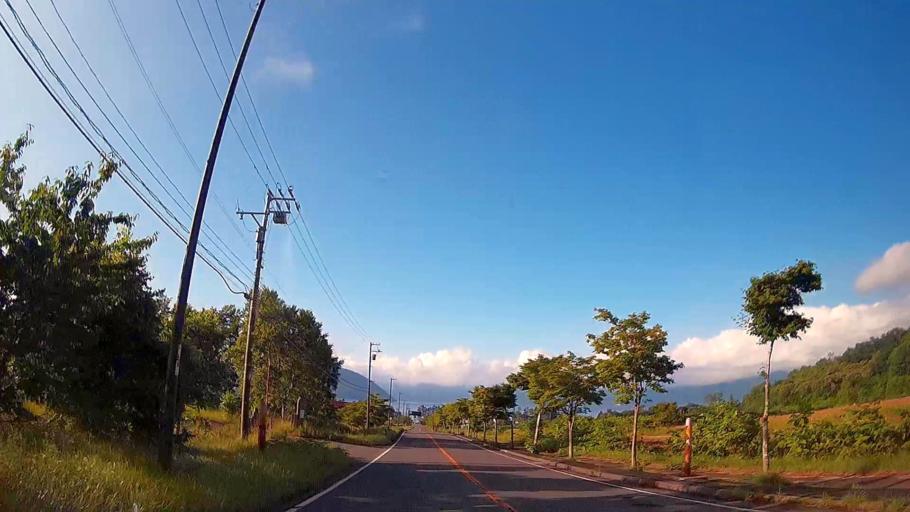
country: JP
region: Hokkaido
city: Date
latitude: 42.5528
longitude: 140.8622
